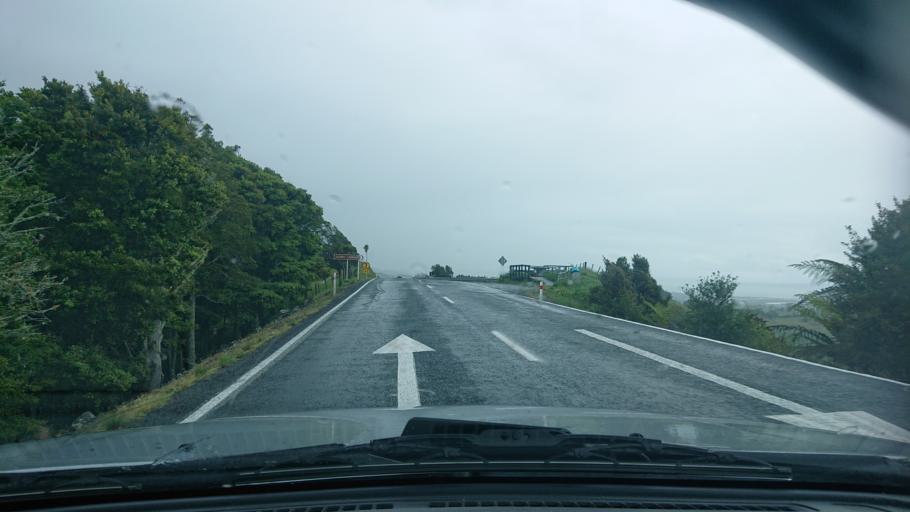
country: NZ
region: Auckland
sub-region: Auckland
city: Wellsford
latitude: -36.3513
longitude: 174.4719
